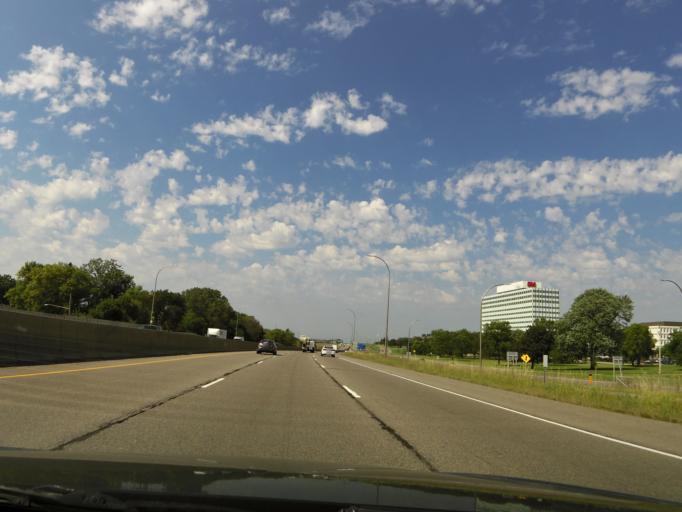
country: US
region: Minnesota
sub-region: Ramsey County
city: Maplewood
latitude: 44.9487
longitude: -92.9902
